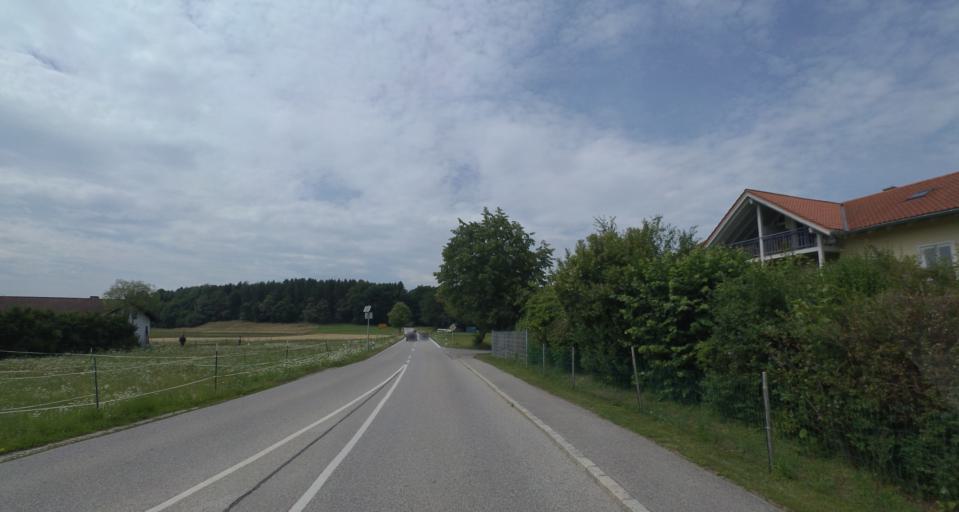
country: DE
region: Bavaria
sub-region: Upper Bavaria
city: Chieming
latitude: 47.9132
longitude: 12.5570
